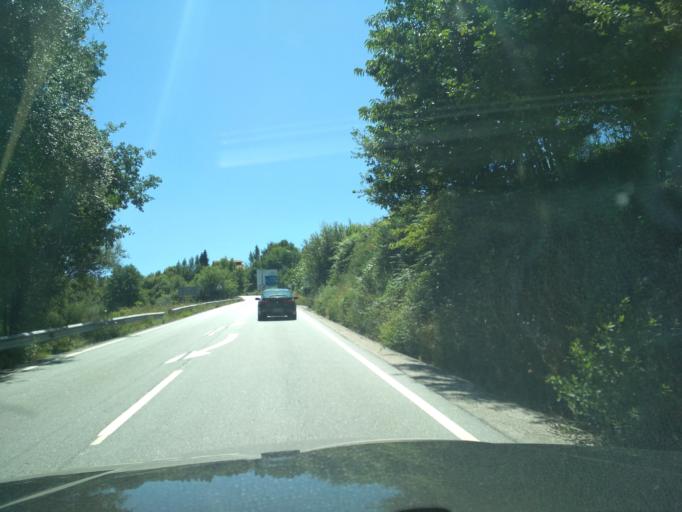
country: PT
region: Vila Real
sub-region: Ribeira de Pena
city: Ribeira de Pena
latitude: 41.5045
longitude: -7.7946
